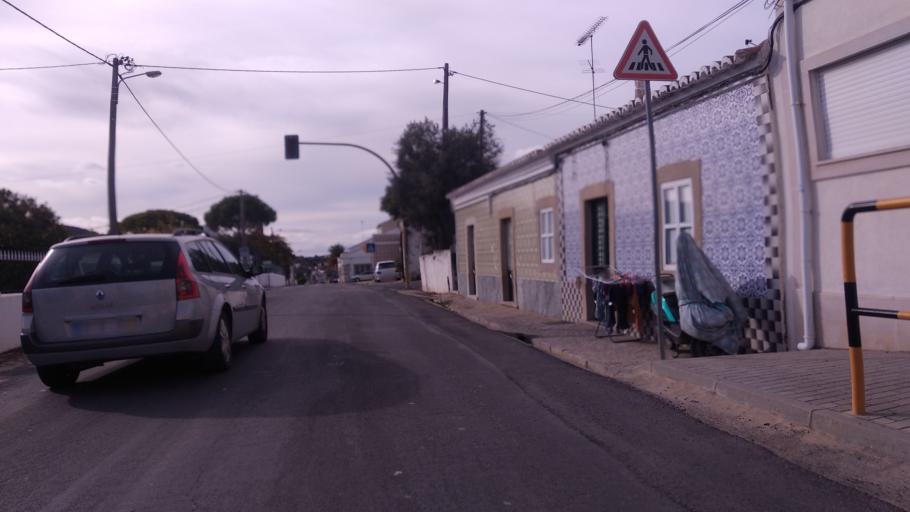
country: PT
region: Faro
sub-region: Sao Bras de Alportel
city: Sao Bras de Alportel
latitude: 37.1522
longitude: -7.9193
